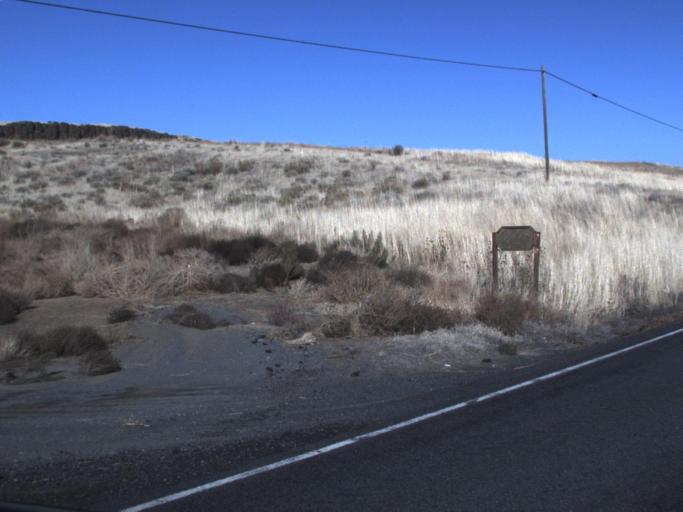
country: US
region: Washington
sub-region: Franklin County
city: Connell
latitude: 46.6507
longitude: -118.5038
